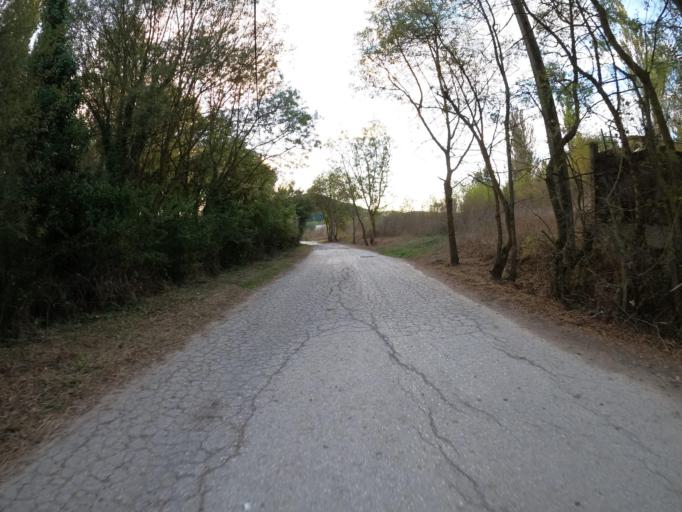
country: ES
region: Navarre
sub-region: Provincia de Navarra
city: Egues-Uharte
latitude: 42.8351
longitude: -1.5811
